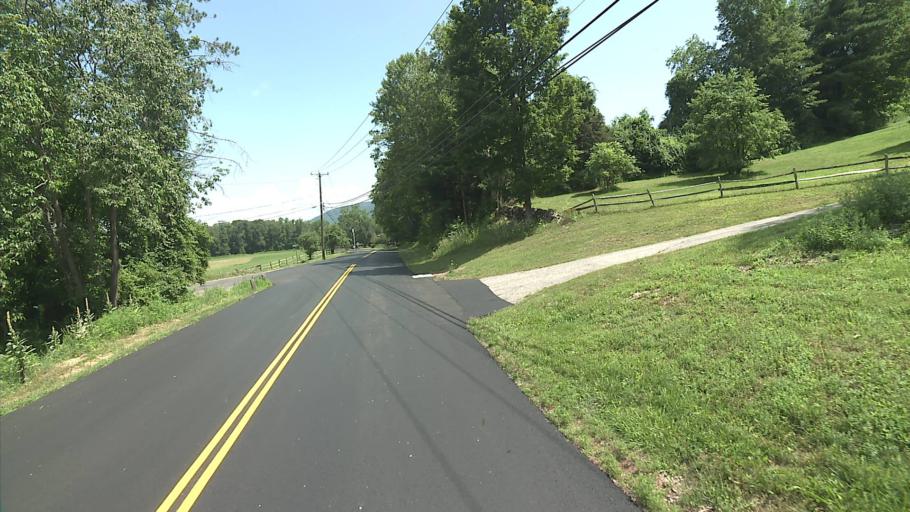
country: US
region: Connecticut
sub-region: Litchfield County
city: Canaan
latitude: 41.9640
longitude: -73.3613
